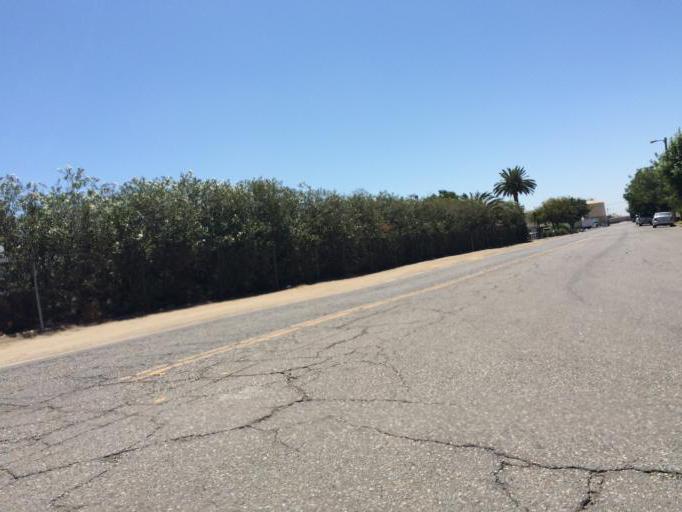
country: US
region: California
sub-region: Fresno County
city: Fresno
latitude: 36.7048
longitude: -119.7548
